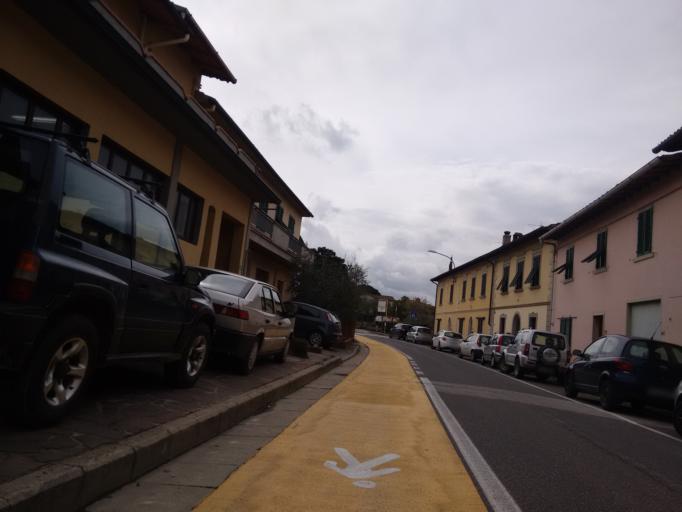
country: IT
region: Tuscany
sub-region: Province of Florence
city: Strada in Chianti
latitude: 43.6627
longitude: 11.2944
